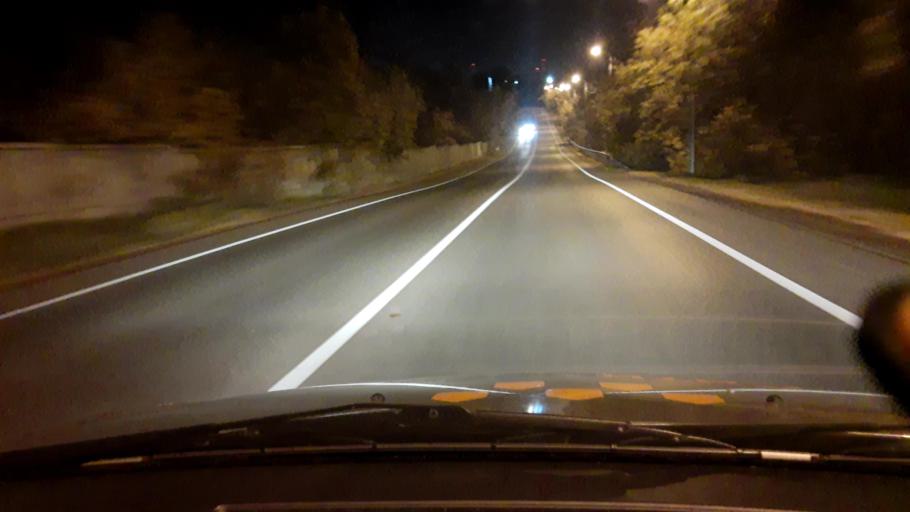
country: RU
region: Bashkortostan
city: Ufa
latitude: 54.8631
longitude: 56.0739
